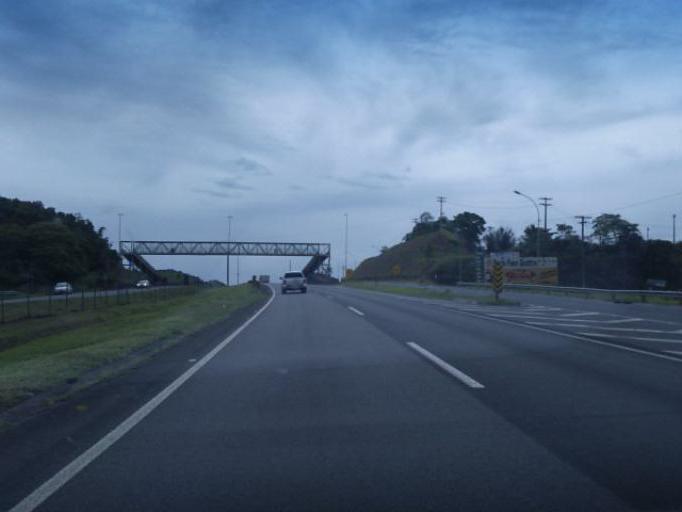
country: BR
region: Sao Paulo
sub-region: Juquia
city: Juquia
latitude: -24.3295
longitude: -47.6207
